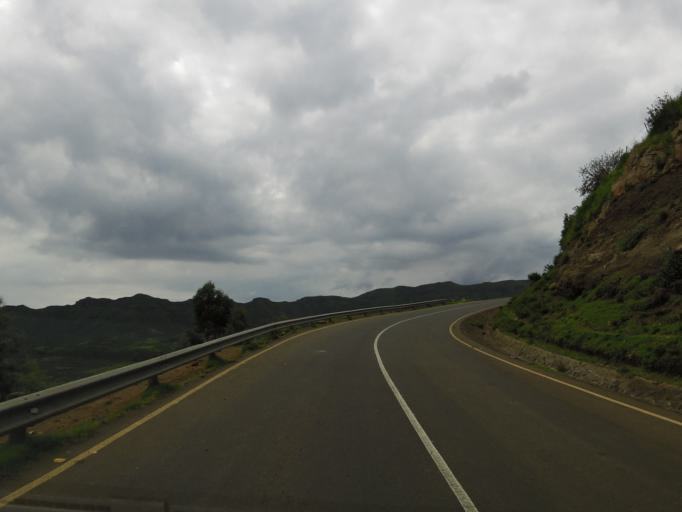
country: LS
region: Butha-Buthe
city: Butha-Buthe
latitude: -29.0362
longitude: 28.2936
